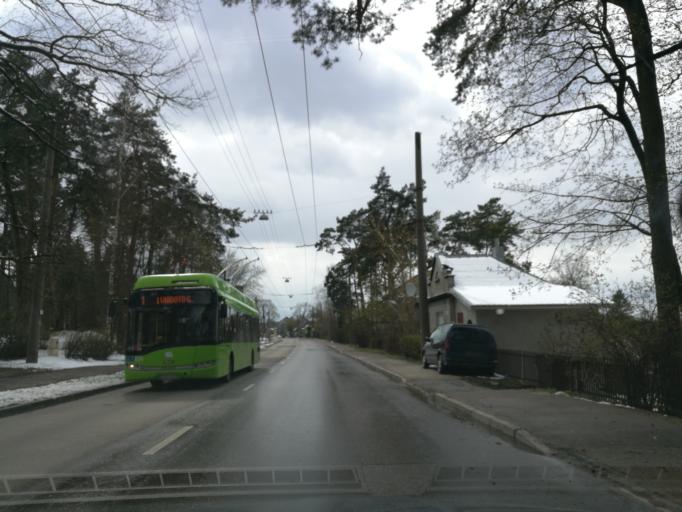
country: LT
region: Kauno apskritis
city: Dainava (Kaunas)
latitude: 54.8695
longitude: 23.9757
